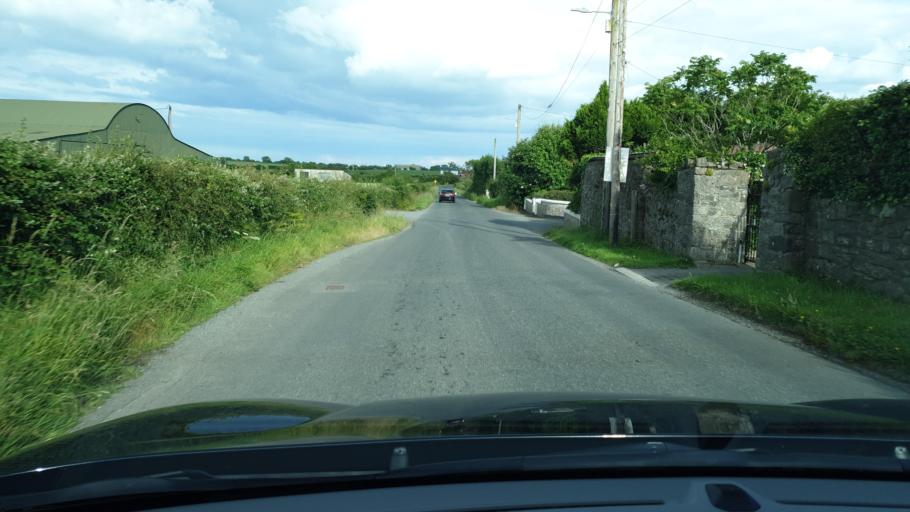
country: IE
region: Leinster
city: Balrothery
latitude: 53.5596
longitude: -6.1745
